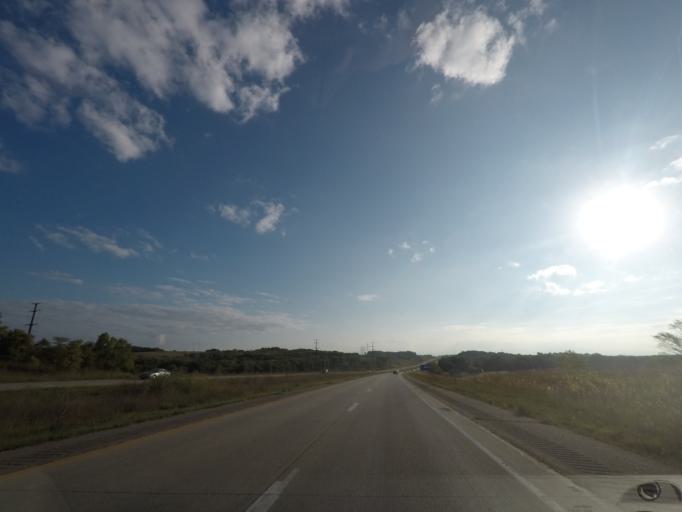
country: US
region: Iowa
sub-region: Warren County
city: Norwalk
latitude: 41.5020
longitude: -93.5945
